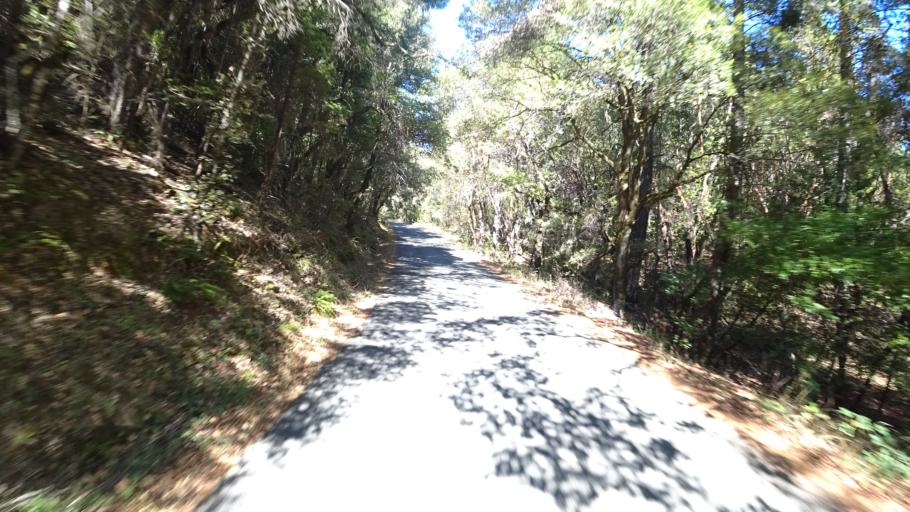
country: US
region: California
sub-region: Siskiyou County
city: Happy Camp
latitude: 41.3808
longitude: -123.4927
